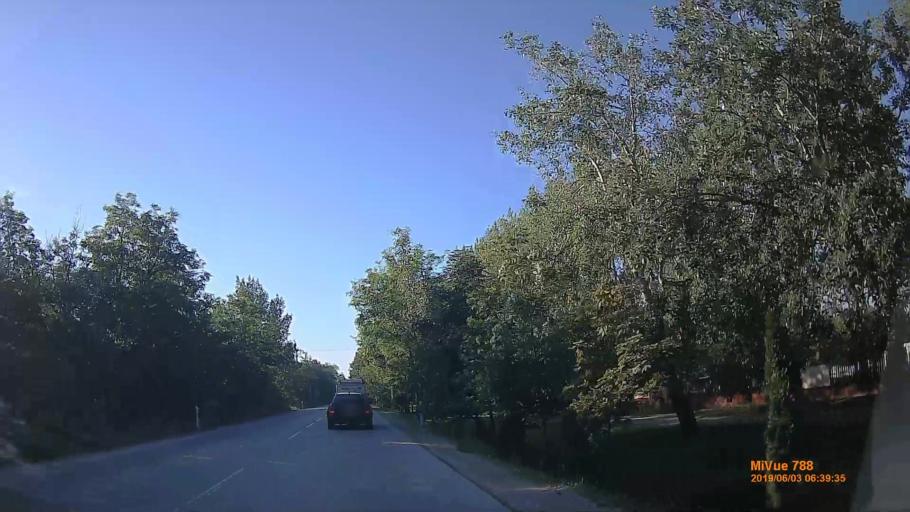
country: HU
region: Pest
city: Dunavarsany
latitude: 47.2860
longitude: 19.1026
